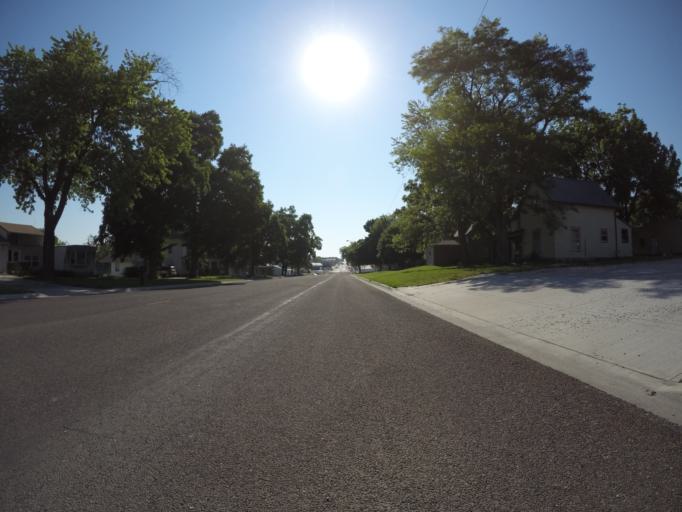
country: US
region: Kansas
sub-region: Brown County
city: Hiawatha
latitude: 39.8529
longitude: -95.5450
